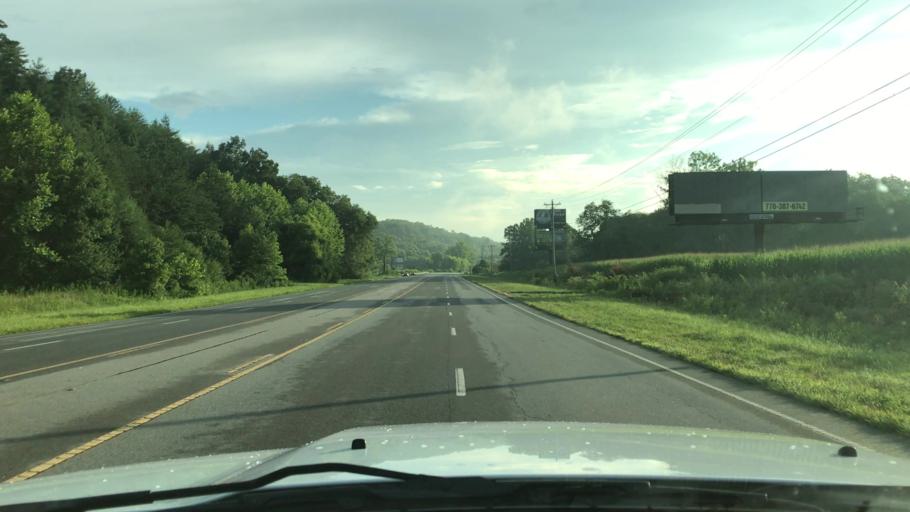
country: US
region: North Carolina
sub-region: Cherokee County
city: Murphy
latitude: 34.9925
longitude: -84.1624
